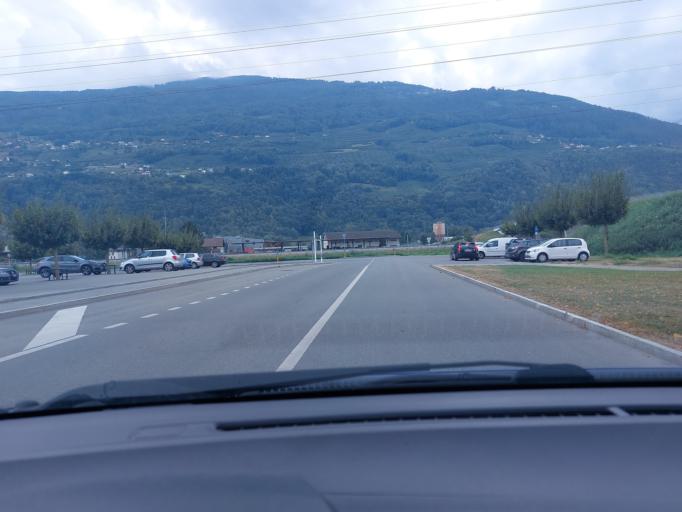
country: CH
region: Valais
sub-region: Sion District
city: Sitten
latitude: 46.2191
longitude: 7.3359
